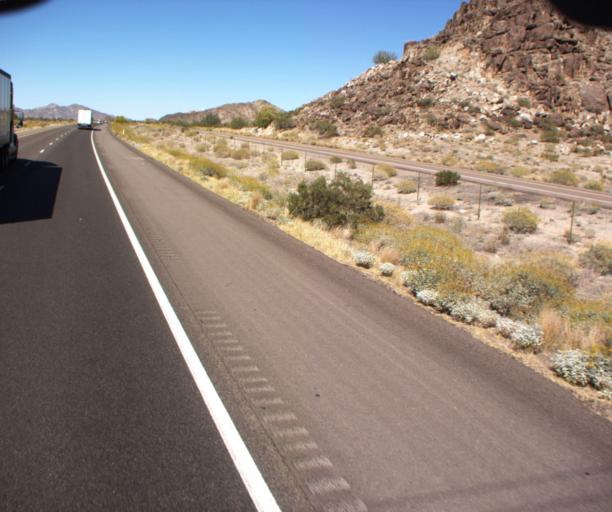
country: US
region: Arizona
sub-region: Maricopa County
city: Buckeye
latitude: 33.1714
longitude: -112.6503
